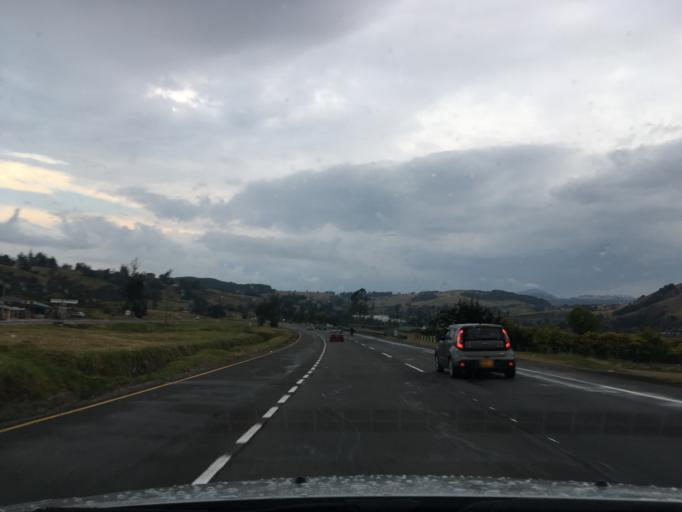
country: CO
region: Cundinamarca
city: Choconta
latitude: 5.1134
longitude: -73.6993
